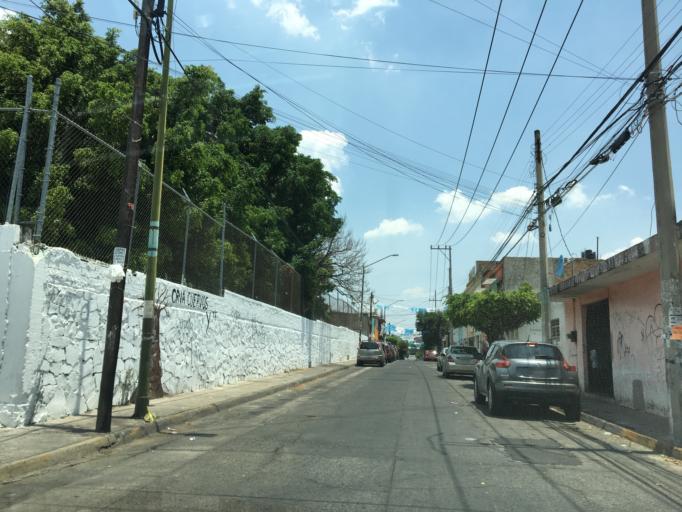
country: MX
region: Jalisco
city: Guadalajara
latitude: 20.6539
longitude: -103.3665
